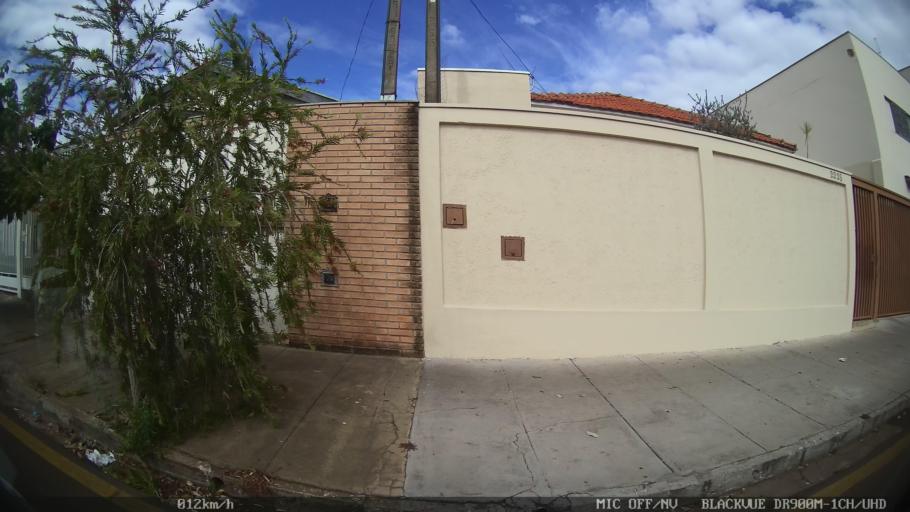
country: BR
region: Sao Paulo
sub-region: Bady Bassitt
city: Bady Bassitt
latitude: -20.8135
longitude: -49.5104
